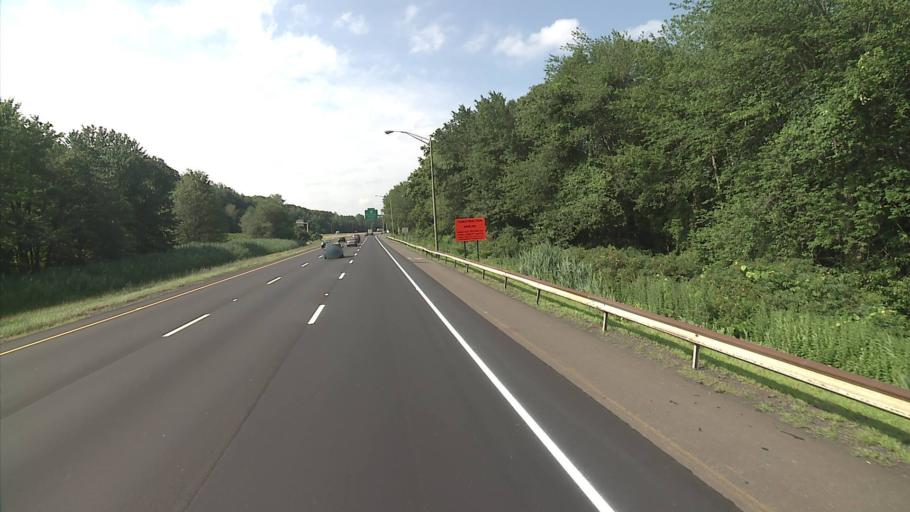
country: US
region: Connecticut
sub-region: New Haven County
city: North Haven
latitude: 41.4100
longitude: -72.8326
